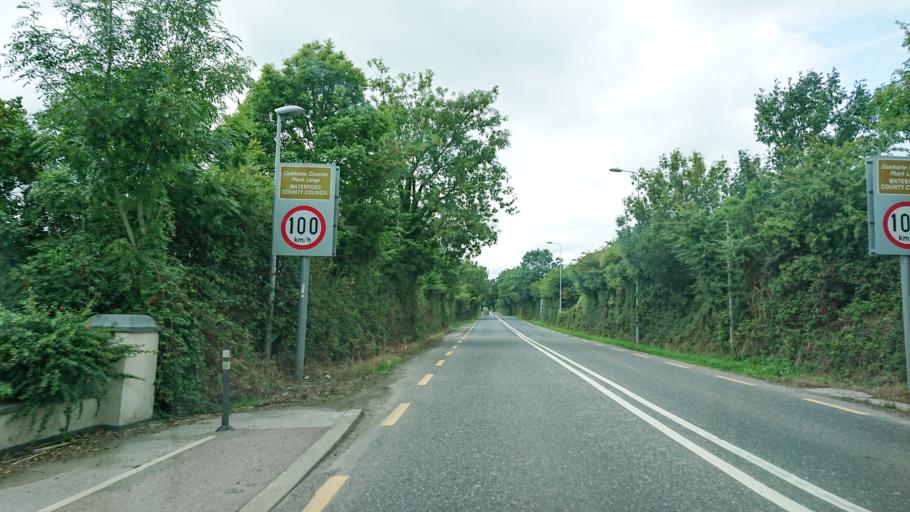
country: IE
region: Munster
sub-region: Waterford
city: Dungarvan
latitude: 52.1095
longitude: -7.6755
